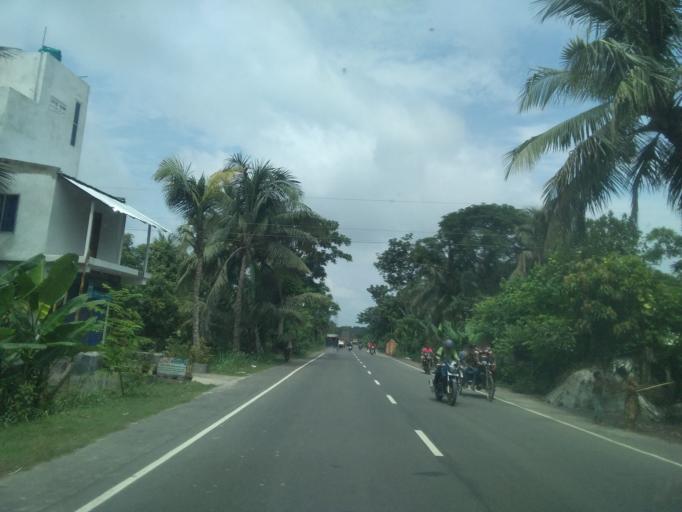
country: BD
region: Khulna
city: Kesabpur
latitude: 22.8167
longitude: 89.2567
